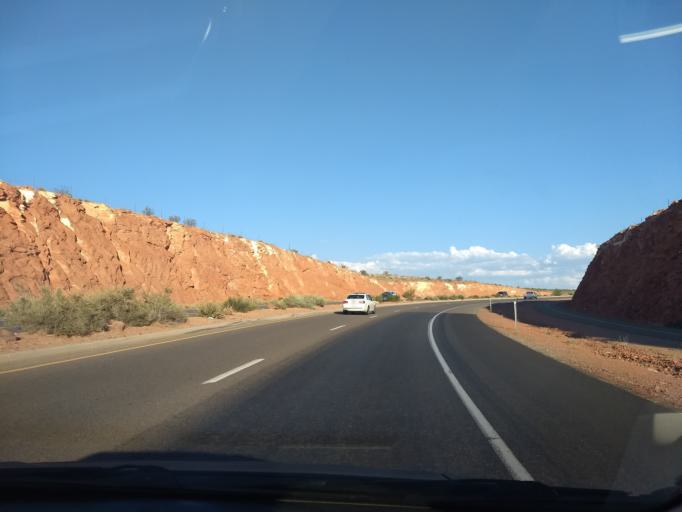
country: US
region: Utah
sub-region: Washington County
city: Saint George
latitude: 37.1318
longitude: -113.5843
